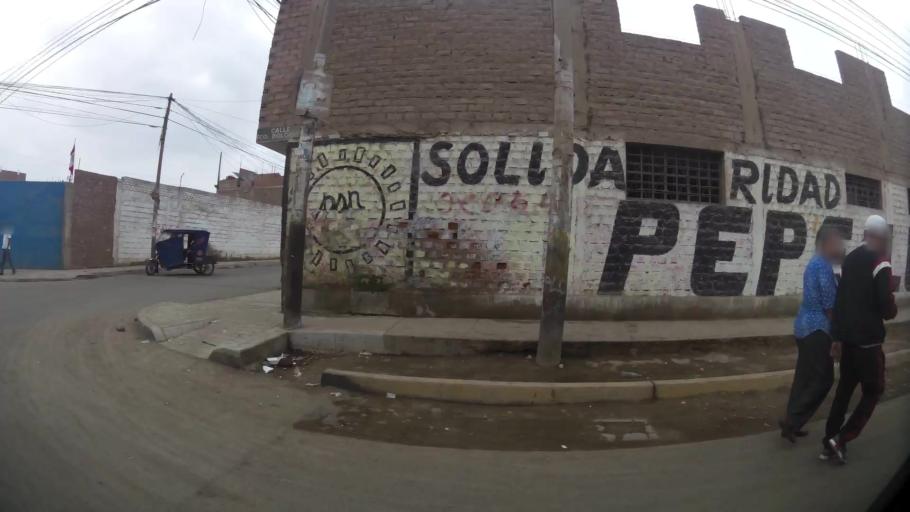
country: PE
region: Lima
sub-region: Provincia de Huaral
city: Huaral
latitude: -11.4974
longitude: -77.2017
